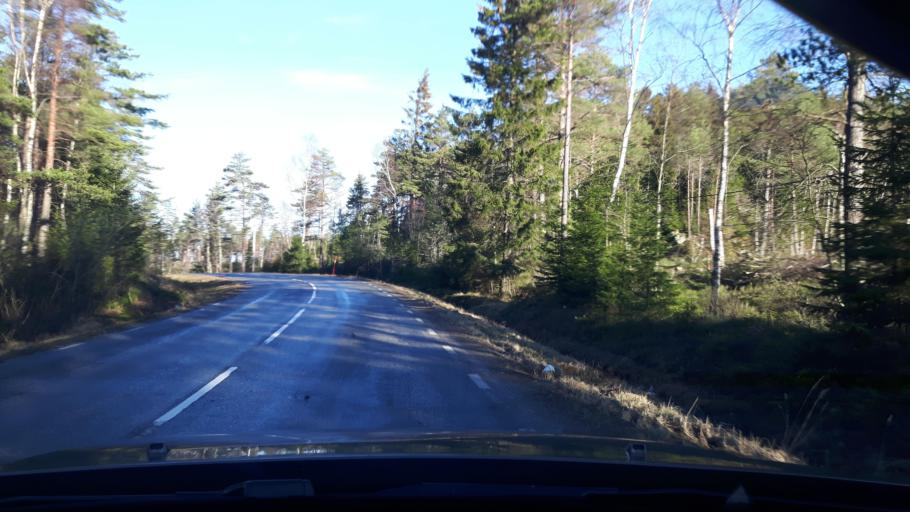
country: SE
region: Vaestra Goetaland
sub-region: Munkedals Kommun
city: Munkedal
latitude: 58.5156
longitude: 11.6840
